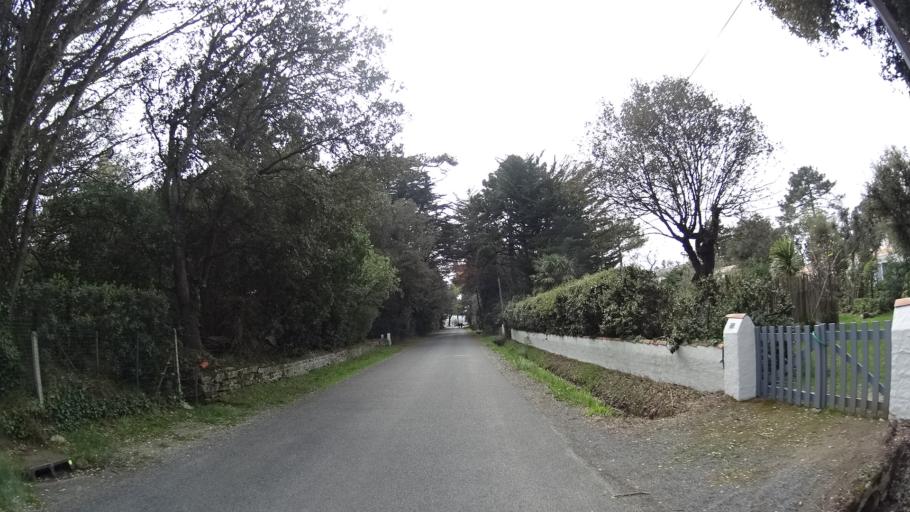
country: FR
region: Pays de la Loire
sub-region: Departement de la Vendee
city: La Gueriniere
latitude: 47.0114
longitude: -2.2294
